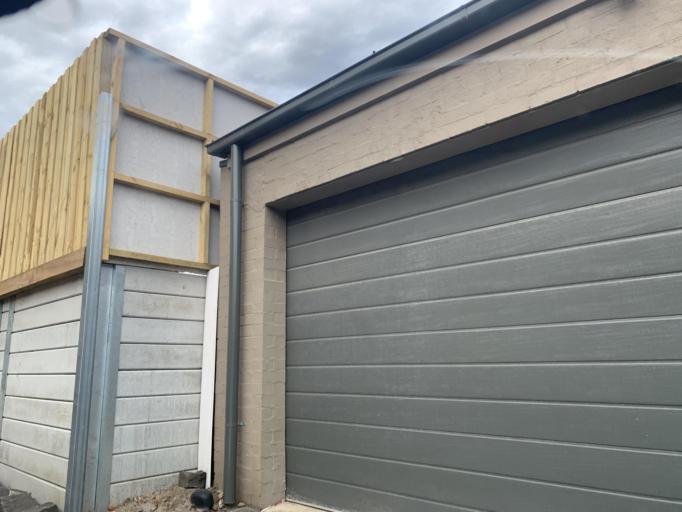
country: AU
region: Victoria
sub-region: Stonnington
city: Malvern East
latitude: -37.8730
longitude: 145.0436
